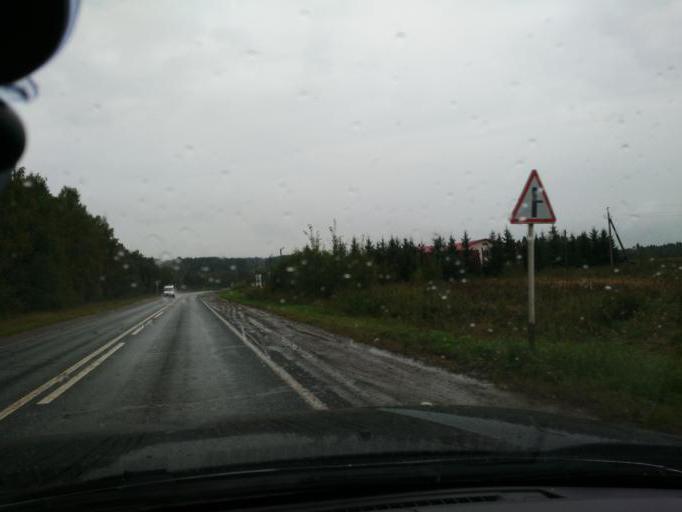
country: RU
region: Perm
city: Yugo-Kamskiy
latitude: 57.5394
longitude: 55.6869
